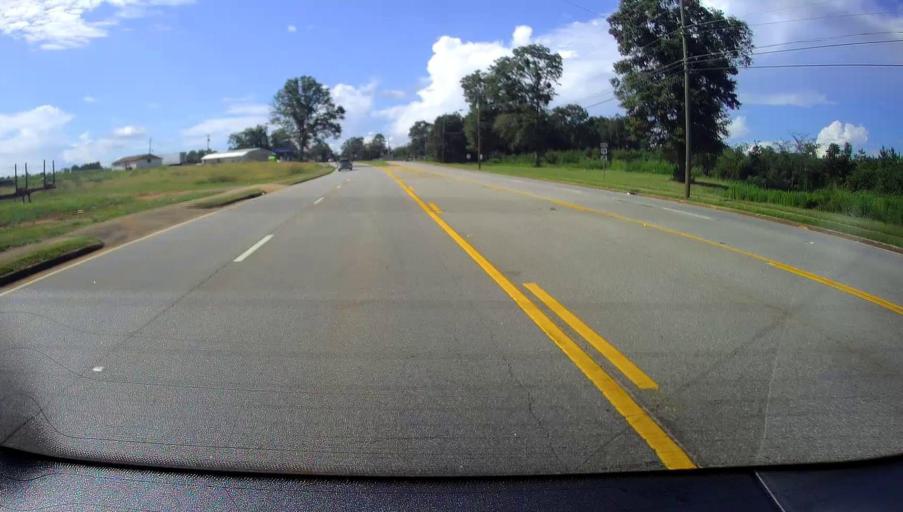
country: US
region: Georgia
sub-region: Upson County
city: Thomaston
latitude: 32.8721
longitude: -84.3236
